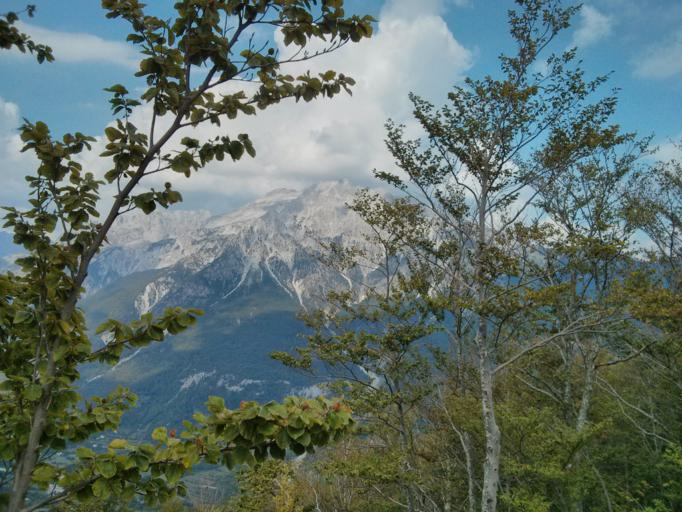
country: AL
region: Shkoder
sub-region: Rrethi i Shkodres
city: Nicaj-Shale
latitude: 42.3862
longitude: 19.7579
